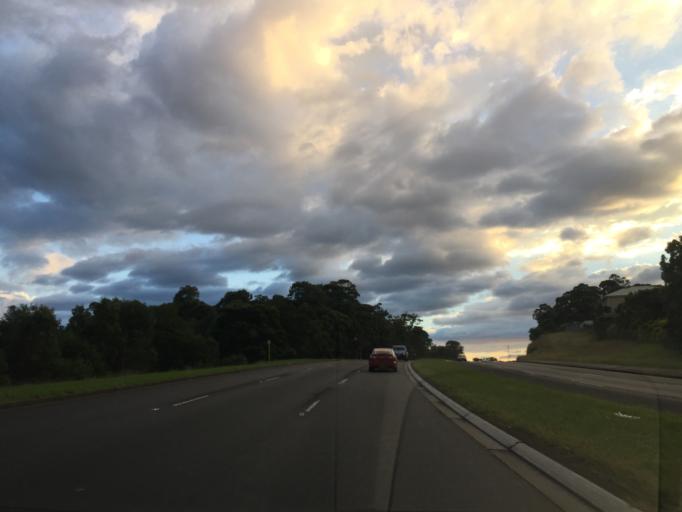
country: AU
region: New South Wales
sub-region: Shellharbour
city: Albion Park Rail
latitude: -34.5689
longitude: 150.8239
